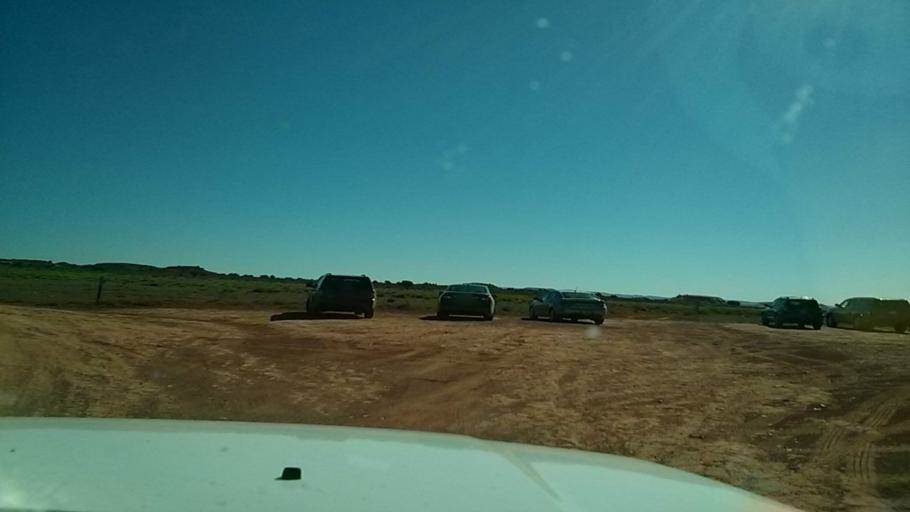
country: US
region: Arizona
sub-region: Coconino County
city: Page
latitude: 37.4654
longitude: -111.2126
